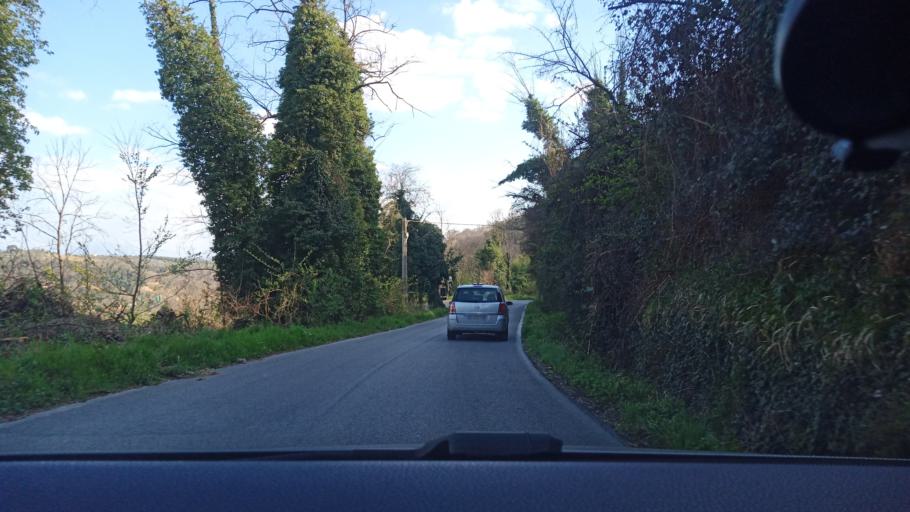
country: IT
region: Latium
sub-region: Citta metropolitana di Roma Capitale
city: Torrita Tiberina
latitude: 42.2411
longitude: 12.6219
